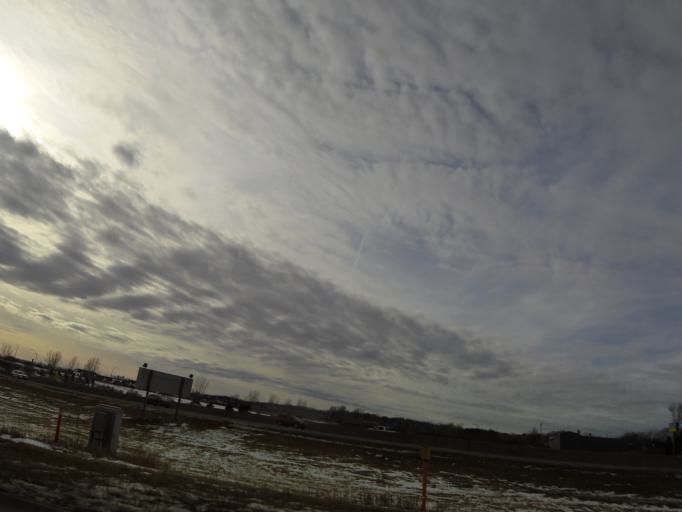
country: US
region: Minnesota
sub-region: Dakota County
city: Burnsville
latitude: 44.7167
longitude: -93.2820
